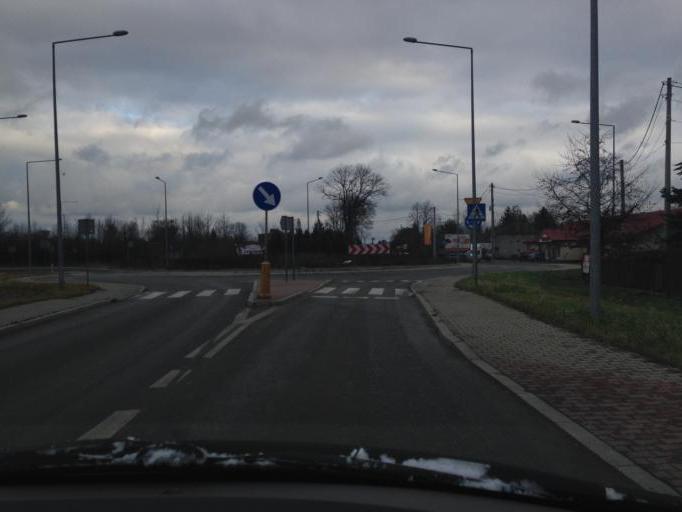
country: PL
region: Lesser Poland Voivodeship
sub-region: Powiat wielicki
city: Gdow
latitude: 49.9078
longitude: 20.1817
